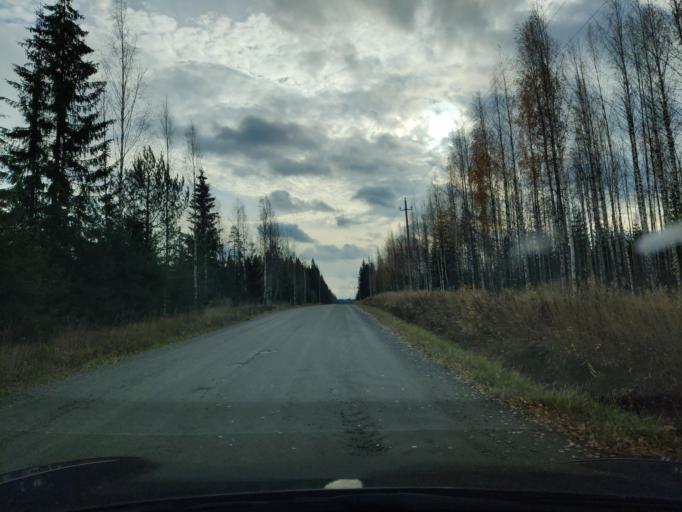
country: FI
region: Northern Savo
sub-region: Kuopio
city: Siilinjaervi
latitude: 63.1125
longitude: 27.5489
